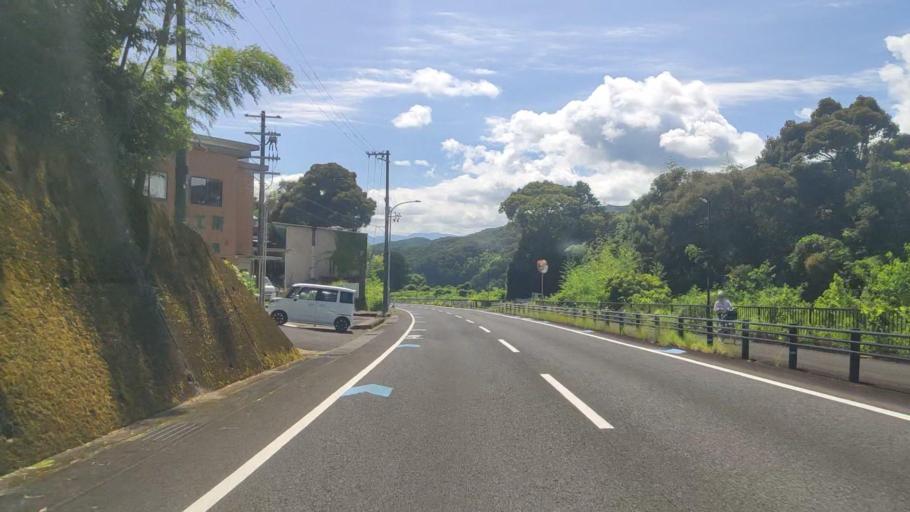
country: JP
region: Wakayama
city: Shingu
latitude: 33.7453
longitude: 136.0117
